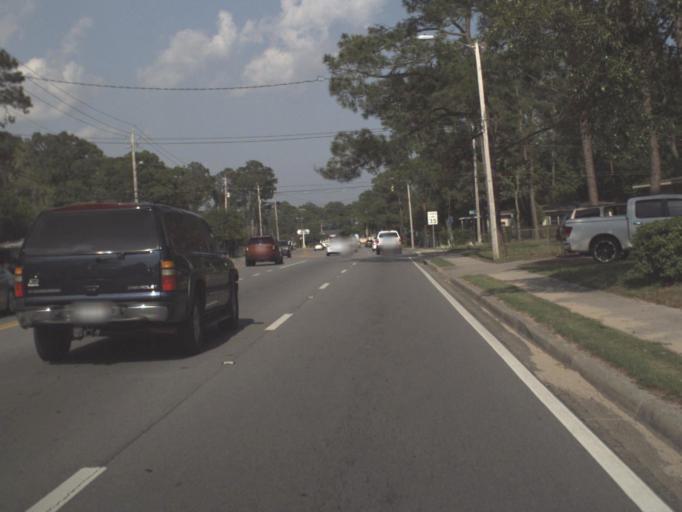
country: US
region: Florida
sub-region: Escambia County
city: Goulding
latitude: 30.4541
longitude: -87.2172
